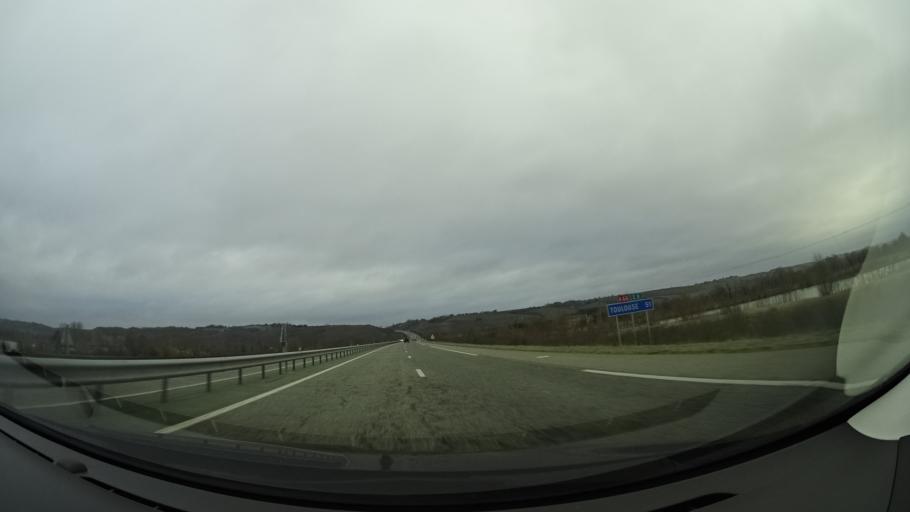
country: FR
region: Midi-Pyrenees
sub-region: Departement de l'Ariege
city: Mazeres
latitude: 43.2616
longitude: 1.6619
